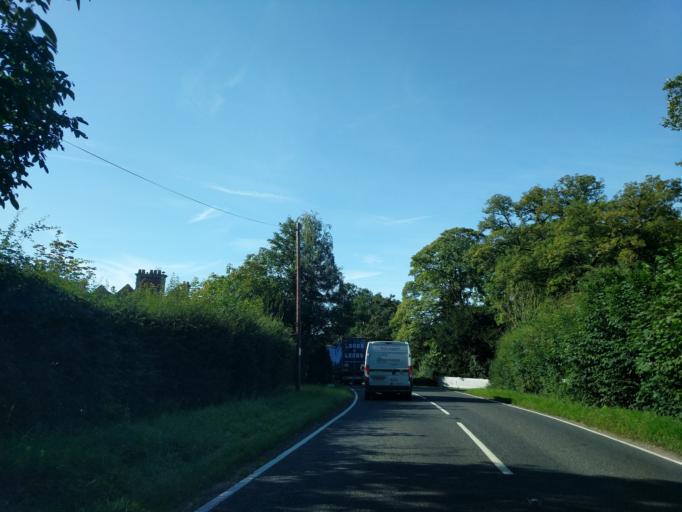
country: GB
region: England
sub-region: Lincolnshire
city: Bourne
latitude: 52.7962
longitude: -0.4502
